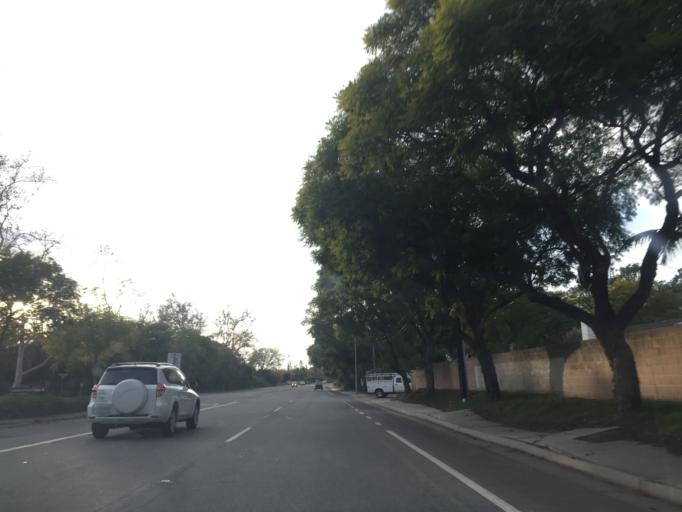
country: US
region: California
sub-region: Santa Barbara County
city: Goleta
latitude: 34.4530
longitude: -119.8107
